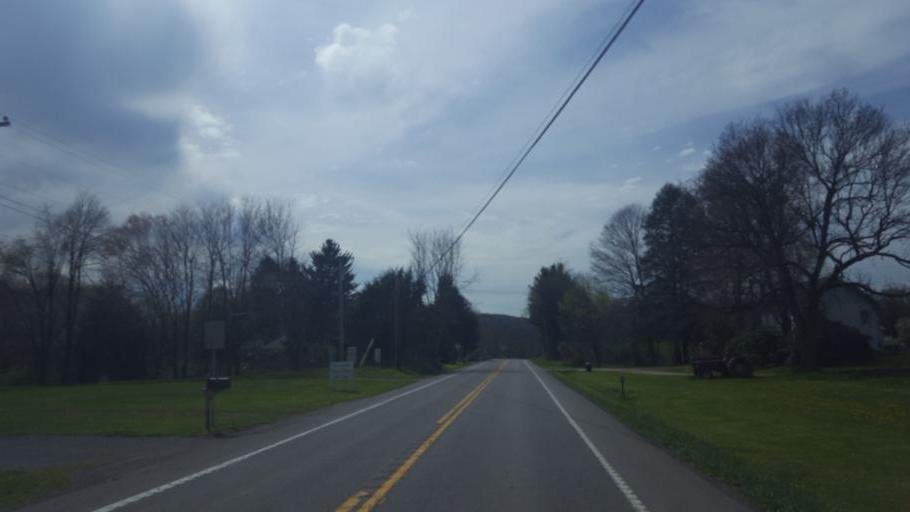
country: US
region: Pennsylvania
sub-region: Mercer County
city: Stoneboro
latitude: 41.3474
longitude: -80.0516
